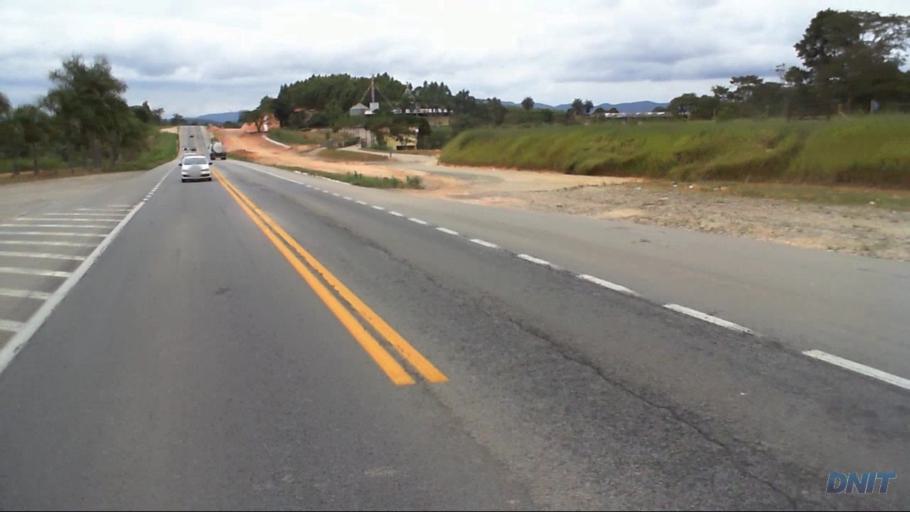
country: BR
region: Minas Gerais
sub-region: Barao De Cocais
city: Barao de Cocais
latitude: -19.7683
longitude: -43.4524
